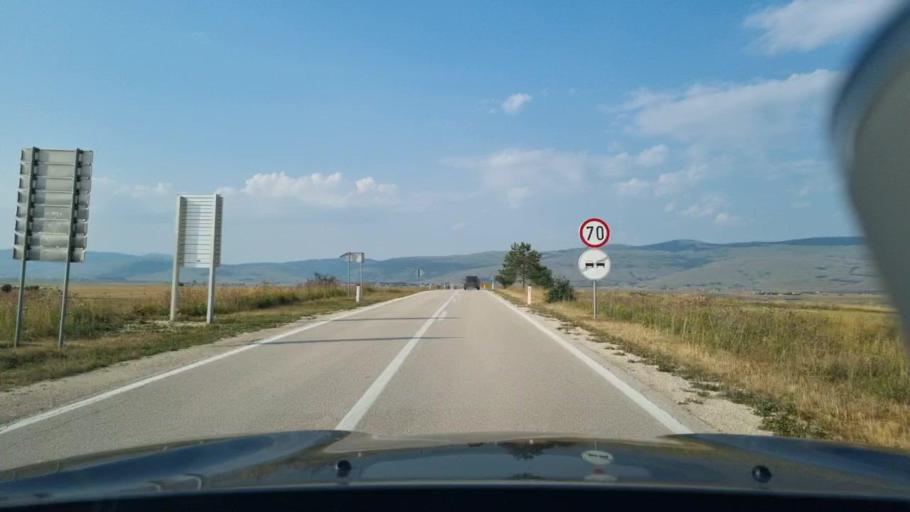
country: BA
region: Federation of Bosnia and Herzegovina
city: Glamoc
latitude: 44.1213
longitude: 16.7986
